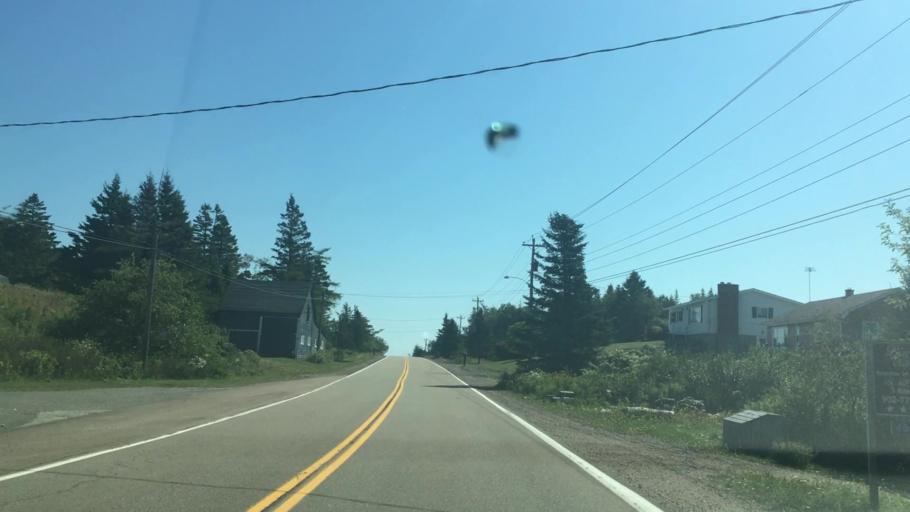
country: CA
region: Nova Scotia
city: Antigonish
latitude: 45.0248
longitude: -62.0248
